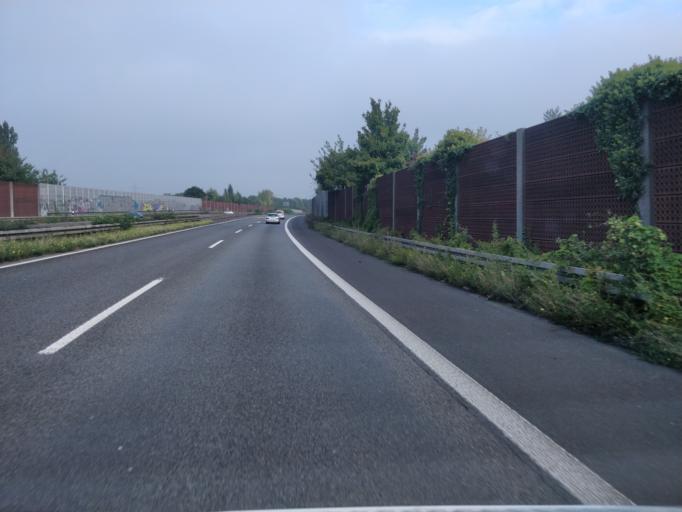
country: DE
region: North Rhine-Westphalia
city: Meiderich
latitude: 51.5093
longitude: 6.7591
